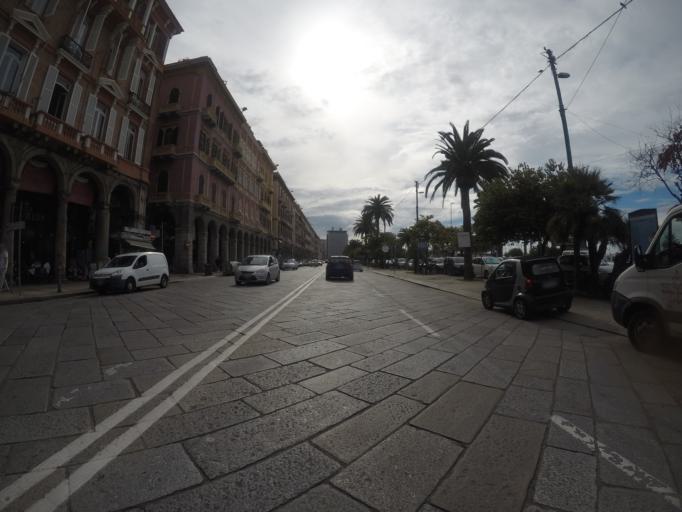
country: IT
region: Sardinia
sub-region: Provincia di Cagliari
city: Cagliari
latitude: 39.2144
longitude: 9.1115
